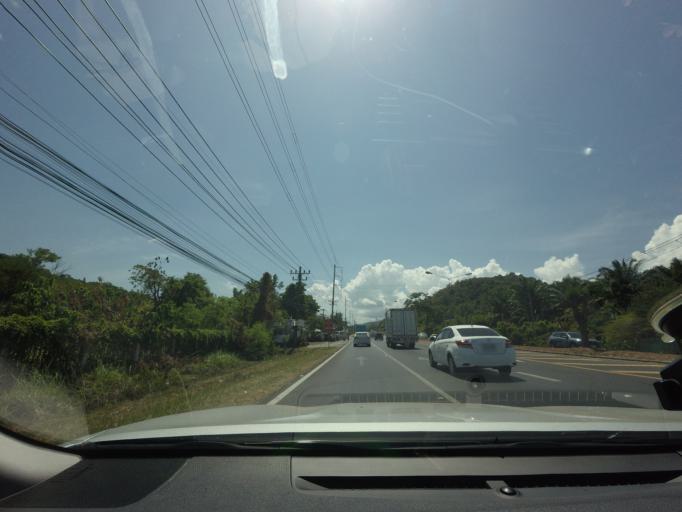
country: TH
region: Phuket
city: Ban Ko Kaeo
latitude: 7.9483
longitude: 98.3854
